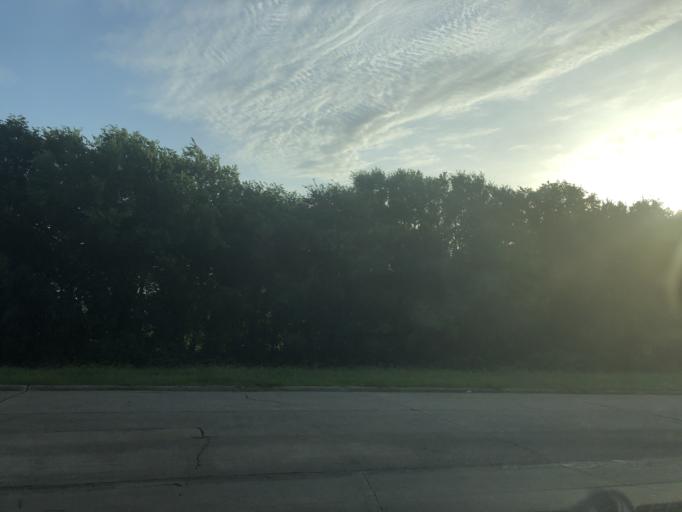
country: US
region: Texas
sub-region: Dallas County
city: Sunnyvale
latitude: 32.8421
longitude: -96.5847
